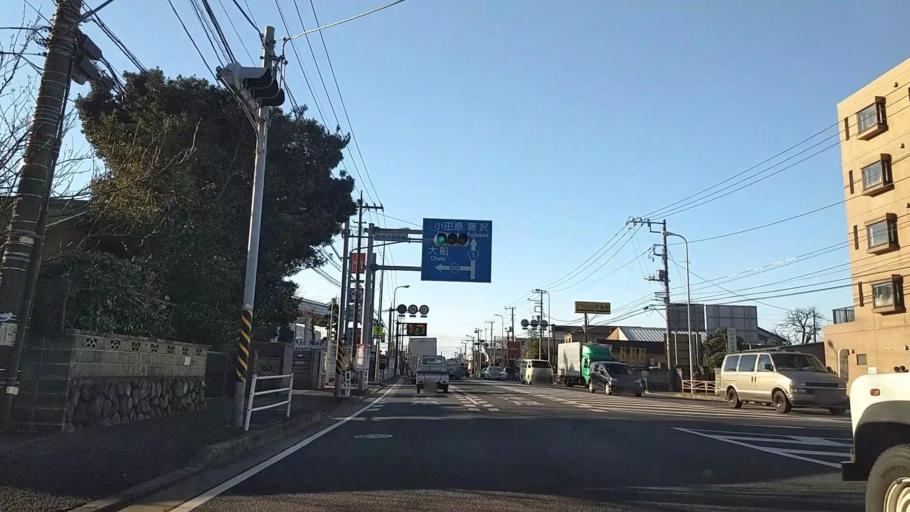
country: JP
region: Kanagawa
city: Fujisawa
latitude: 35.3700
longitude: 139.5007
